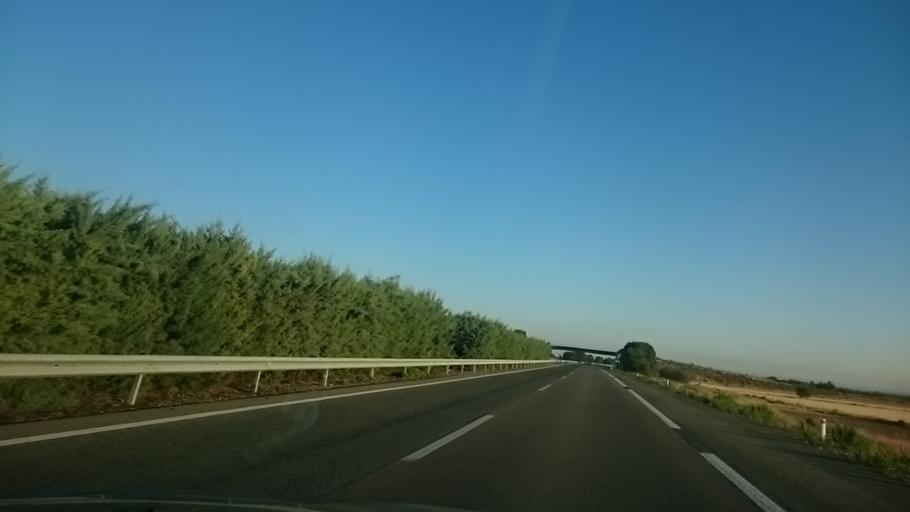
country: ES
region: Navarre
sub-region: Provincia de Navarra
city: Corella
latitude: 42.1114
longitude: -1.7334
